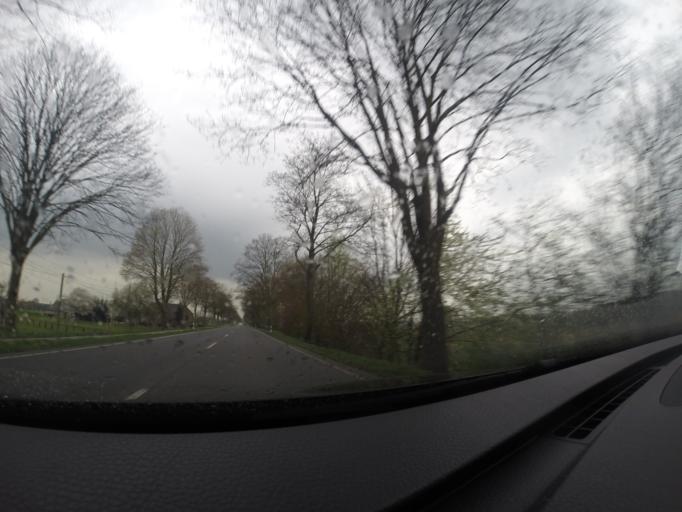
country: DE
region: North Rhine-Westphalia
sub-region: Regierungsbezirk Dusseldorf
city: Uedem
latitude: 51.7079
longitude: 6.3516
